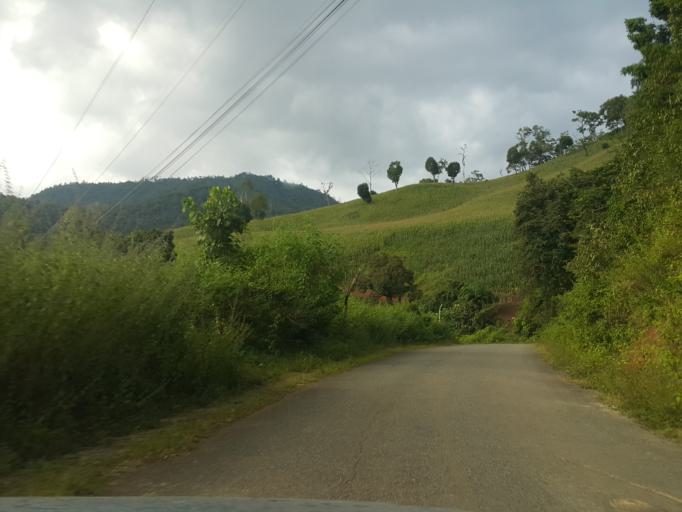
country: TH
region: Mae Hong Son
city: Khun Yuam
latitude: 18.7542
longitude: 98.1913
